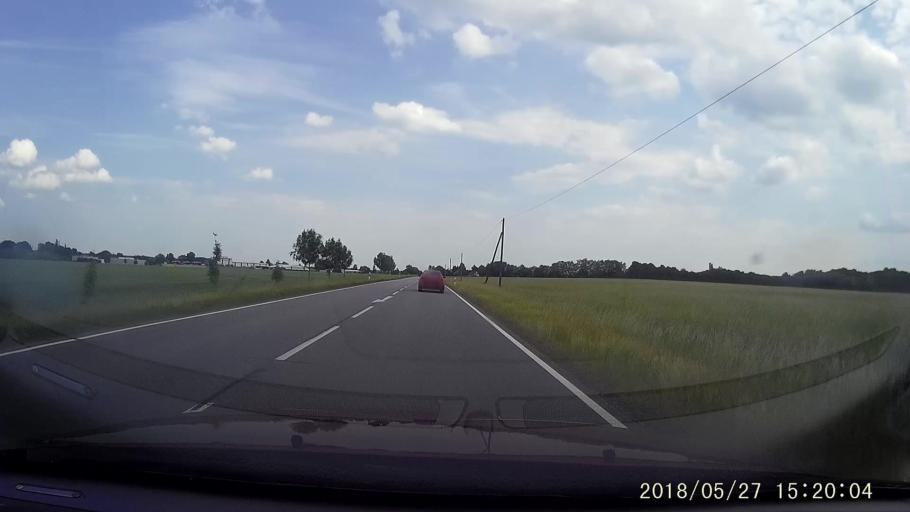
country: DE
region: Saxony
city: Kodersdorf
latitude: 51.2505
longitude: 14.8814
